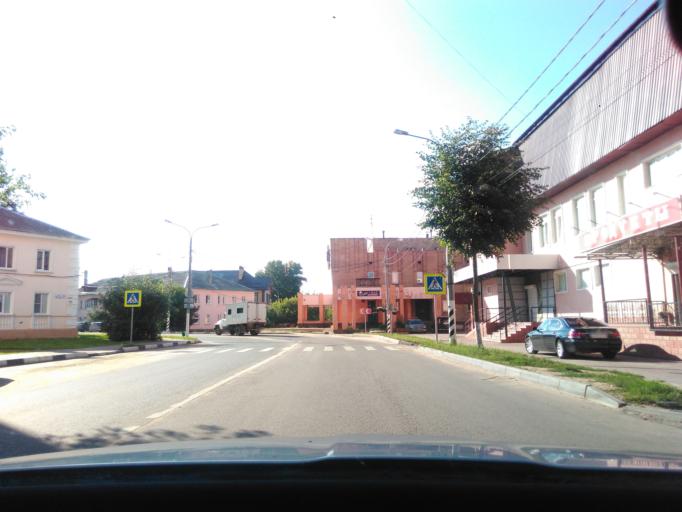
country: RU
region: Moskovskaya
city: Klin
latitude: 56.3377
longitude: 36.7249
